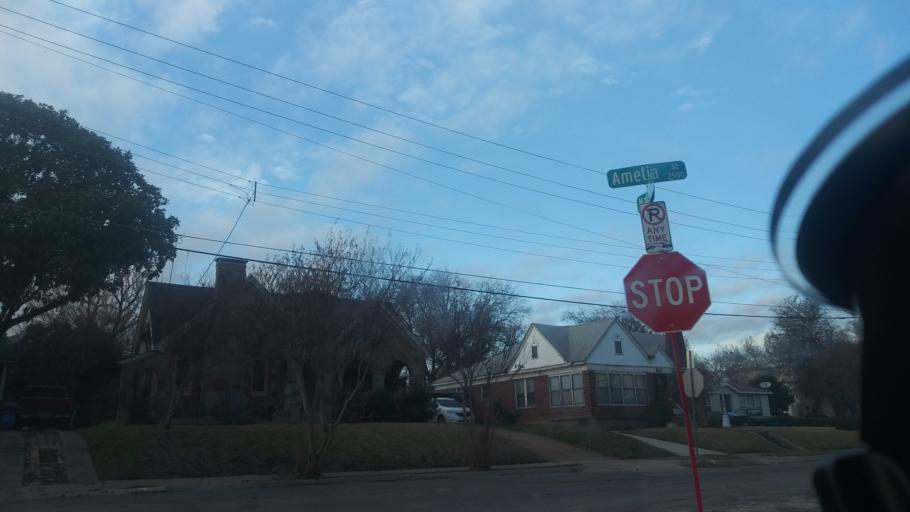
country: US
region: Texas
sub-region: Dallas County
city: Dallas
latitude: 32.8160
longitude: -96.8280
